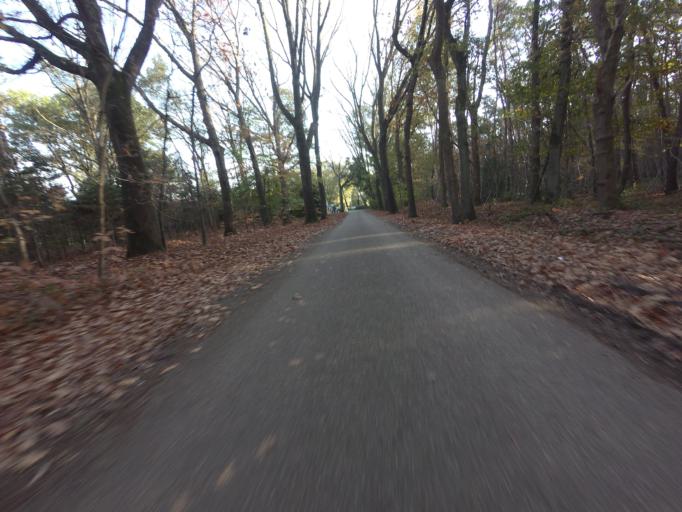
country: DE
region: North Rhine-Westphalia
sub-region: Regierungsbezirk Koln
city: Waldfeucht
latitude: 51.0915
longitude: 6.0083
